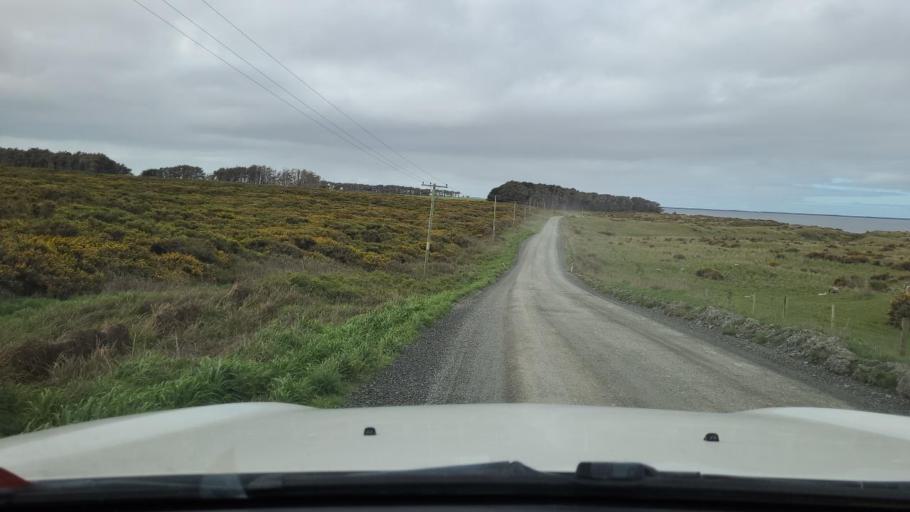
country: NZ
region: Chatham Islands
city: Waitangi
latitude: -43.8278
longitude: -176.4977
